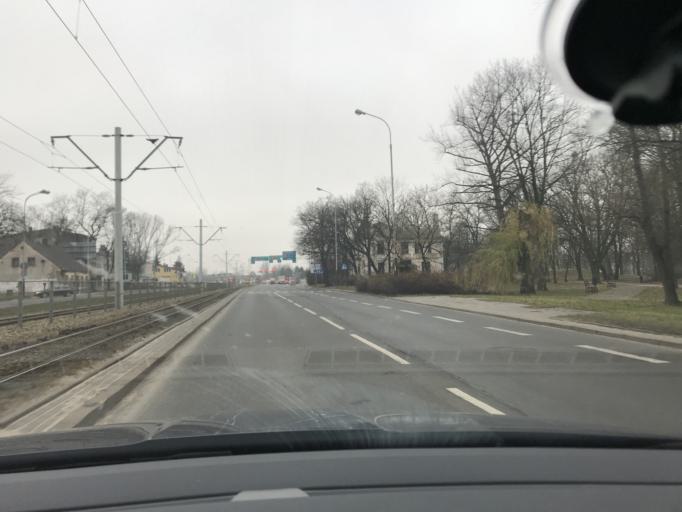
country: PL
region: Lodz Voivodeship
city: Lodz
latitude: 51.7297
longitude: 19.4508
